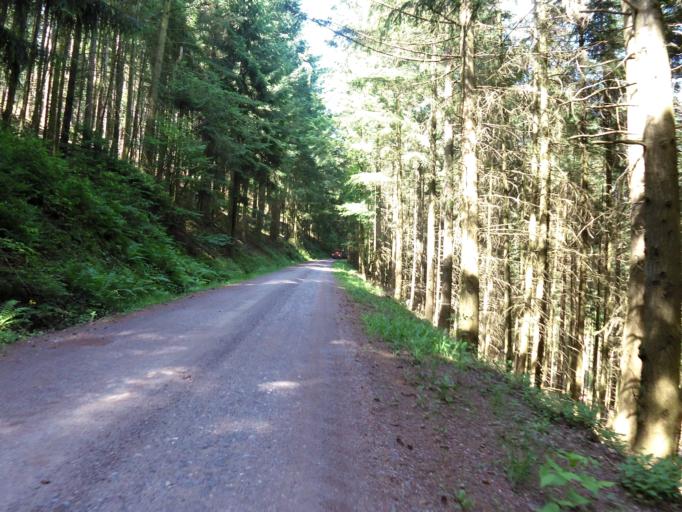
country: DE
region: Rheinland-Pfalz
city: Ramberg
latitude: 49.2930
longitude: 7.9979
